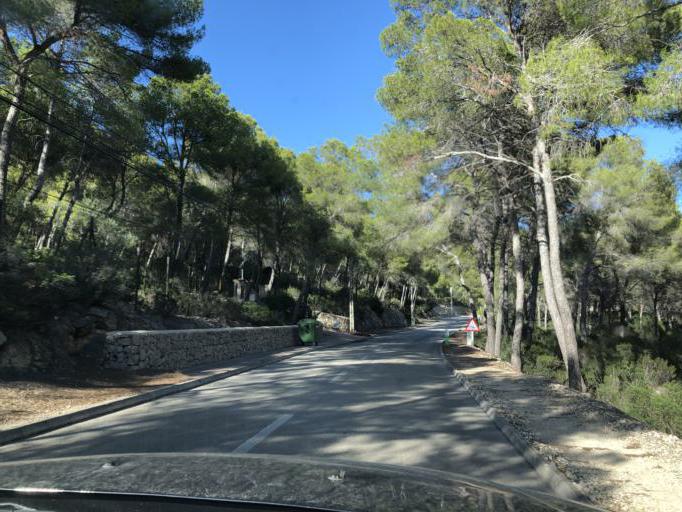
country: ES
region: Balearic Islands
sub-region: Illes Balears
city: Camp de Mar
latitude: 39.5413
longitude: 2.4055
